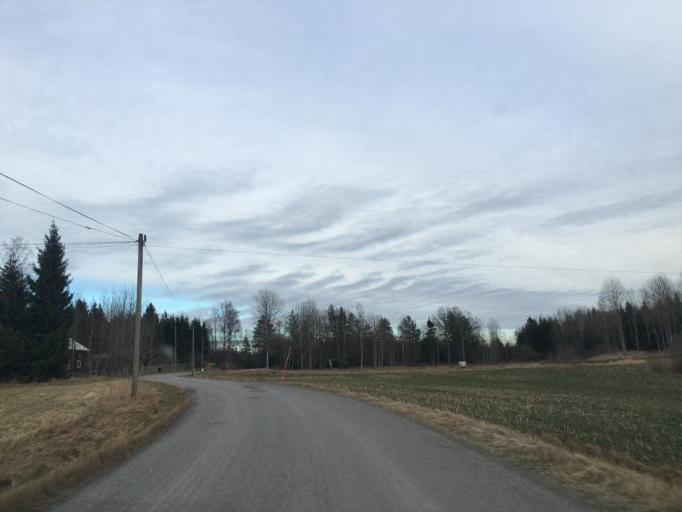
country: SE
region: OEstergoetland
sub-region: Norrkopings Kommun
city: Kimstad
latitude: 58.4275
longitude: 16.0662
